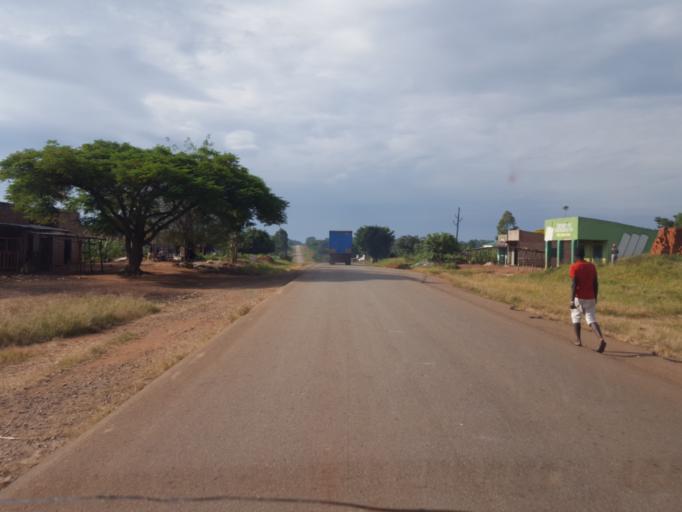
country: UG
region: Central Region
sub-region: Kyankwanzi District
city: Kyankwanzi
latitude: 1.2223
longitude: 31.5495
